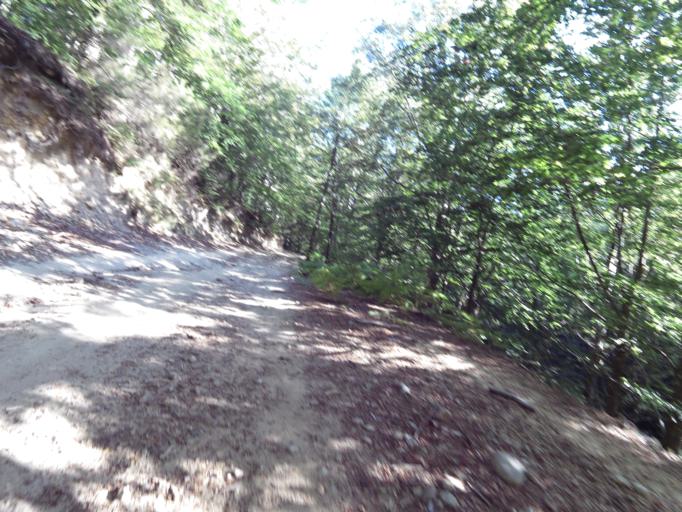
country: IT
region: Calabria
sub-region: Provincia di Vibo-Valentia
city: Nardodipace
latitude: 38.5117
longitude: 16.3773
